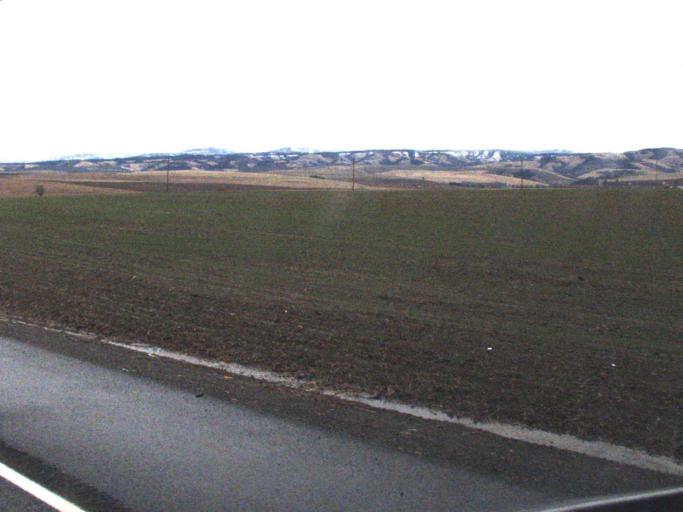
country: US
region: Washington
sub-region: Walla Walla County
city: Walla Walla East
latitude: 46.1016
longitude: -118.2472
